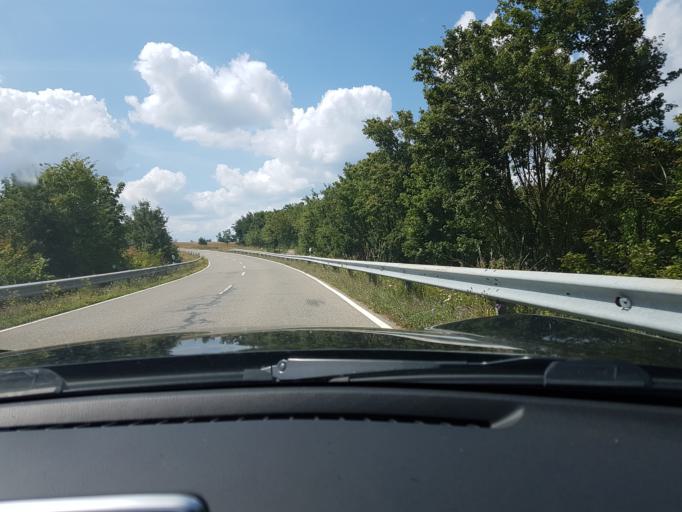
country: DE
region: Baden-Wuerttemberg
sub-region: Karlsruhe Region
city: Limbach
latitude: 49.4264
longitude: 9.2517
